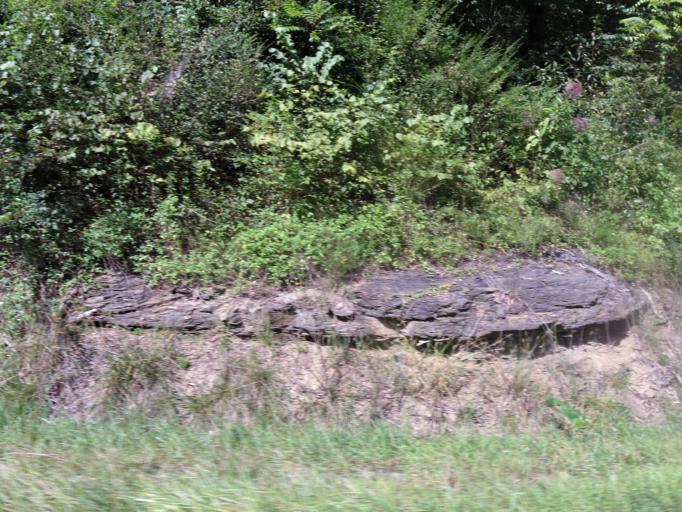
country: US
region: Kentucky
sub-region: Bell County
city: Pineville
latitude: 36.7306
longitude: -83.6669
